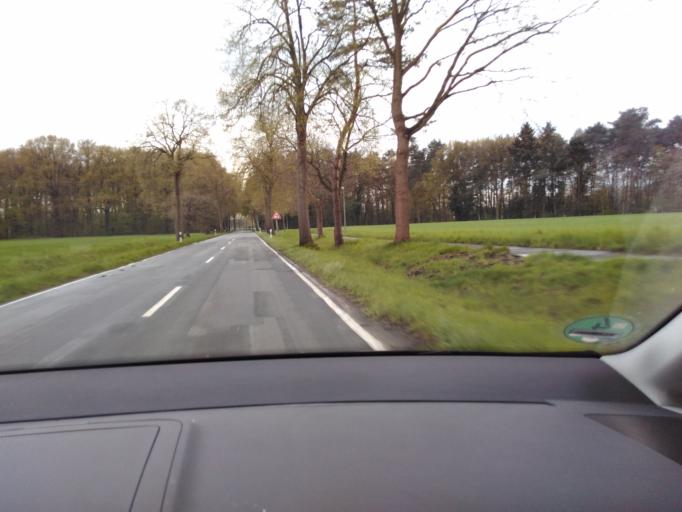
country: DE
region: North Rhine-Westphalia
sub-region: Regierungsbezirk Detmold
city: Verl
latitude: 51.9242
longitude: 8.4878
